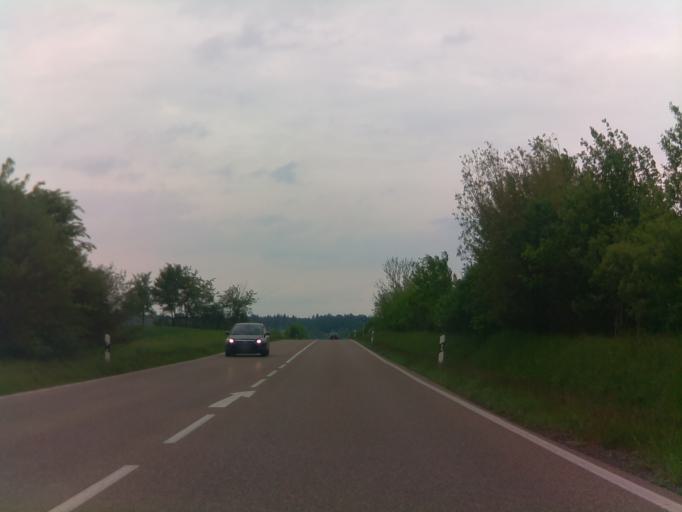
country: DE
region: Baden-Wuerttemberg
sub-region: Tuebingen Region
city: Pliezhausen
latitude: 48.5828
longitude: 9.1717
